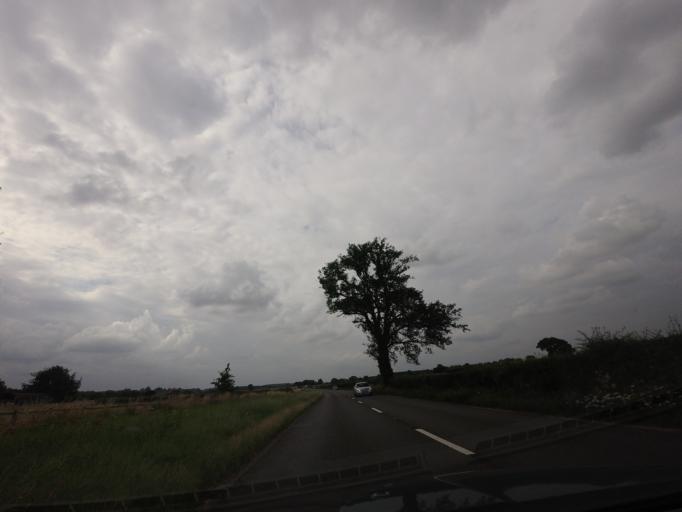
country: GB
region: England
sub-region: Shropshire
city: Tong
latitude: 52.6884
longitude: -2.3139
